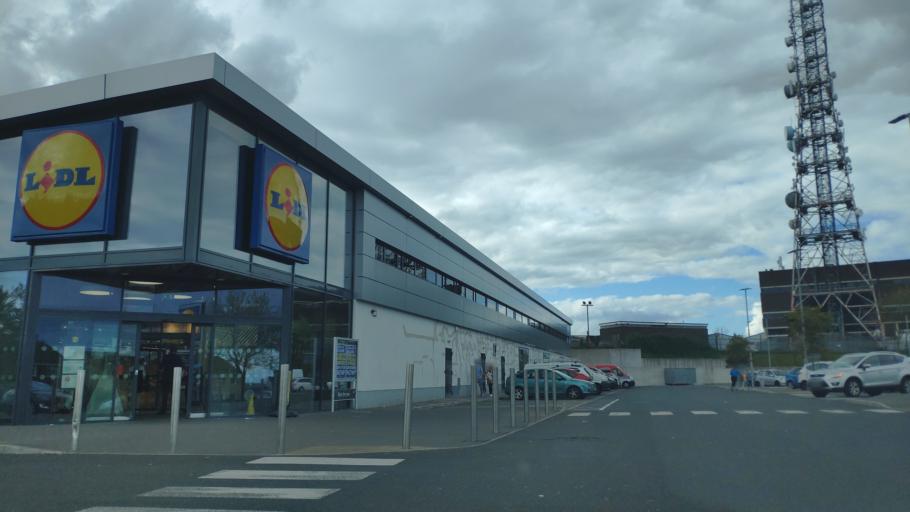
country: IE
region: Munster
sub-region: County Cork
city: Cork
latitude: 51.9114
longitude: -8.4900
